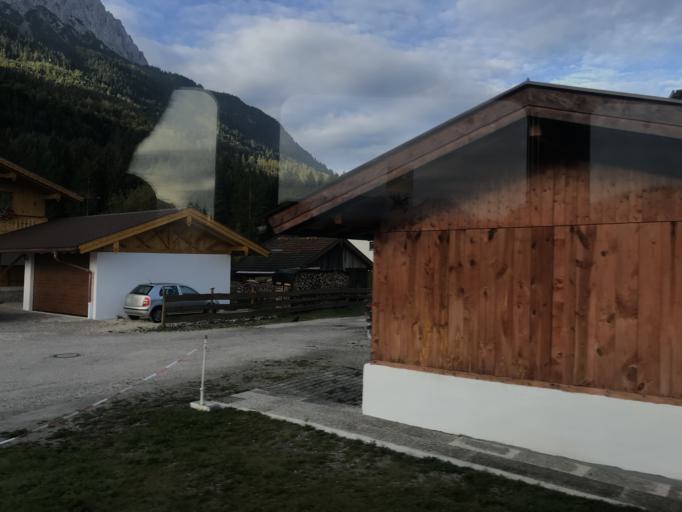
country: DE
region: Bavaria
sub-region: Upper Bavaria
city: Grainau
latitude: 47.4673
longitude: 11.0431
